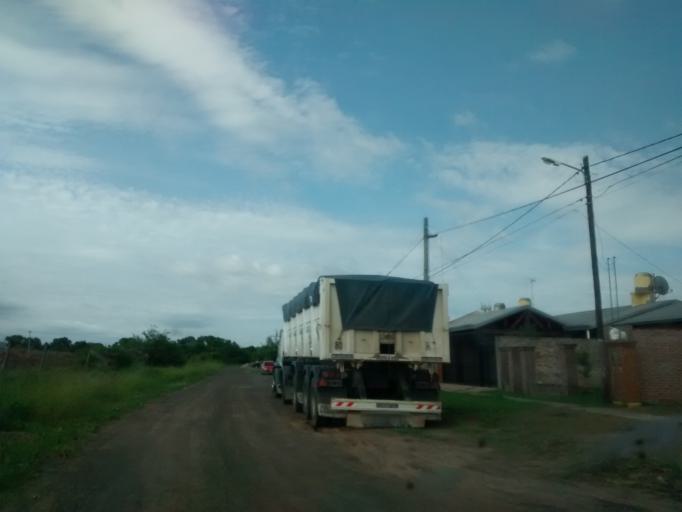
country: AR
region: Chaco
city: Resistencia
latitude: -27.4125
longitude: -58.9624
